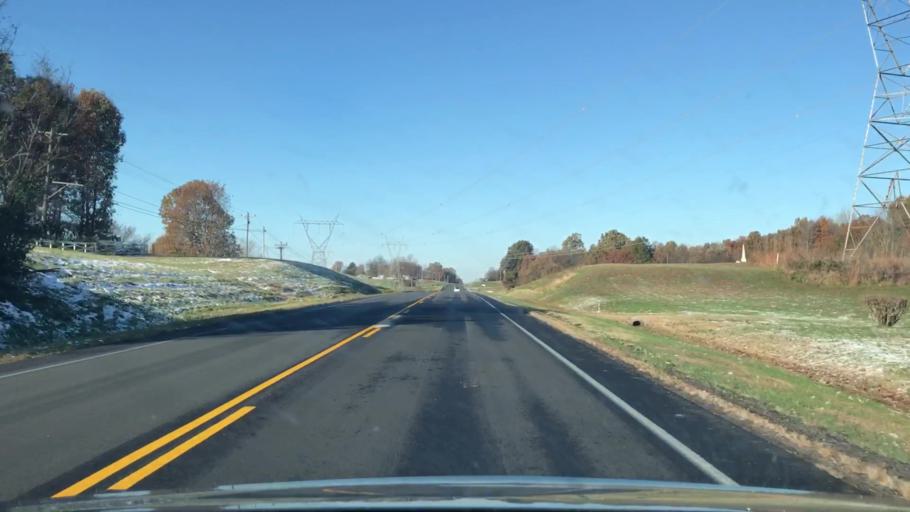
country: US
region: Kentucky
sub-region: Marshall County
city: Calvert City
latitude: 37.0056
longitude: -88.4162
